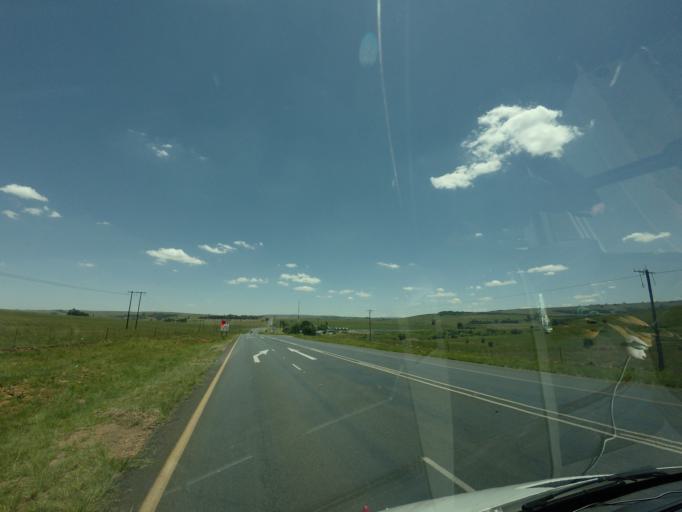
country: ZA
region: Mpumalanga
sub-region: Nkangala District Municipality
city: Belfast
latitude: -25.6855
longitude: 30.2184
